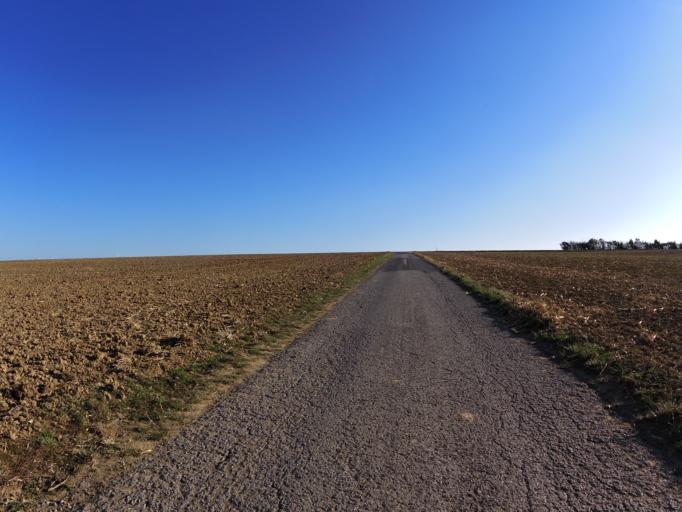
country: DE
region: Bavaria
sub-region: Regierungsbezirk Unterfranken
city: Eibelstadt
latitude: 49.7016
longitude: 9.9837
